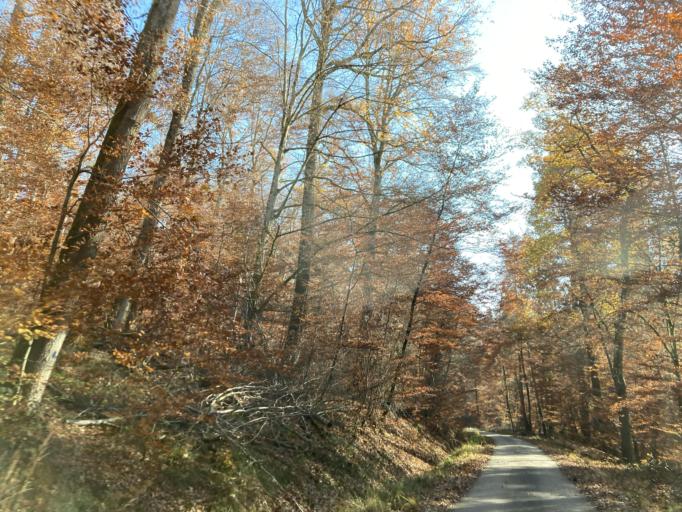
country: DE
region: Baden-Wuerttemberg
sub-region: Tuebingen Region
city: Tuebingen
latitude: 48.5692
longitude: 9.0618
